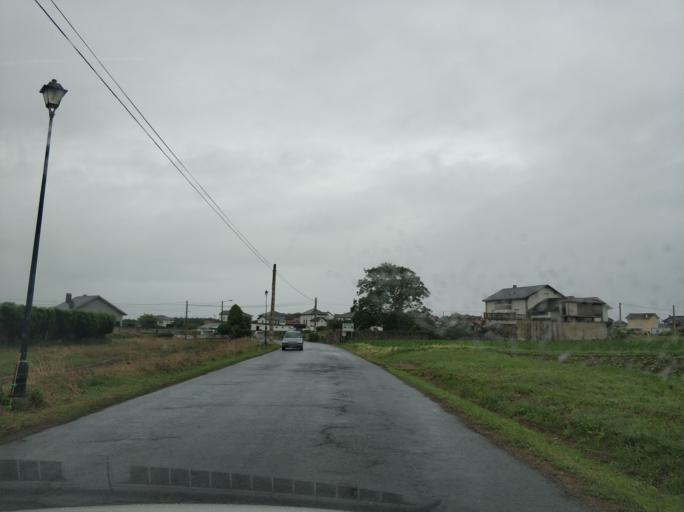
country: ES
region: Asturias
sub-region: Province of Asturias
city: Tineo
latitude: 43.5544
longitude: -6.4612
